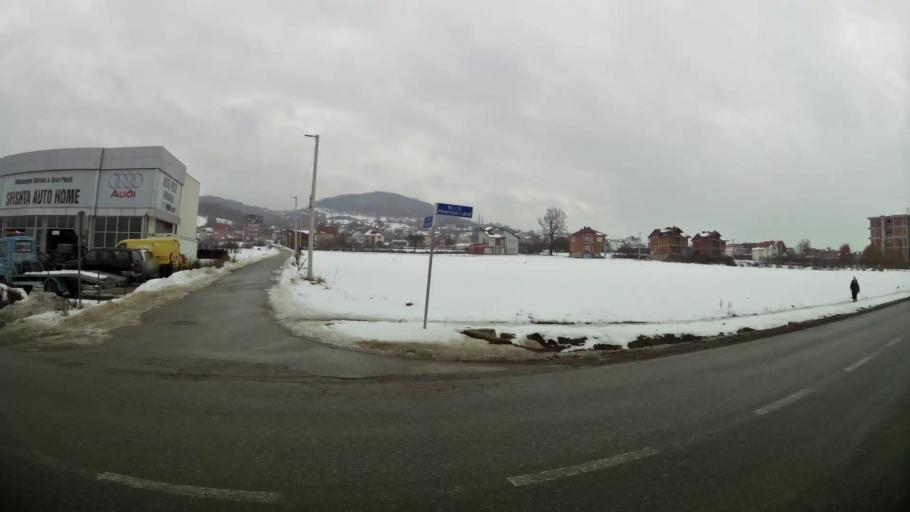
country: XK
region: Pristina
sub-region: Komuna e Prishtines
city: Pristina
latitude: 42.7194
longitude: 21.1479
